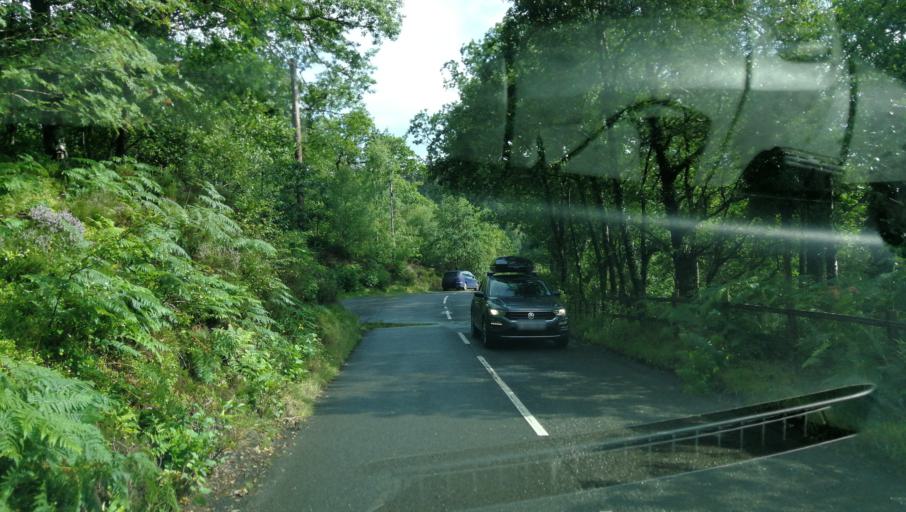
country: GB
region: Scotland
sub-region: Stirling
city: Balfron
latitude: 56.2275
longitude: -4.3849
